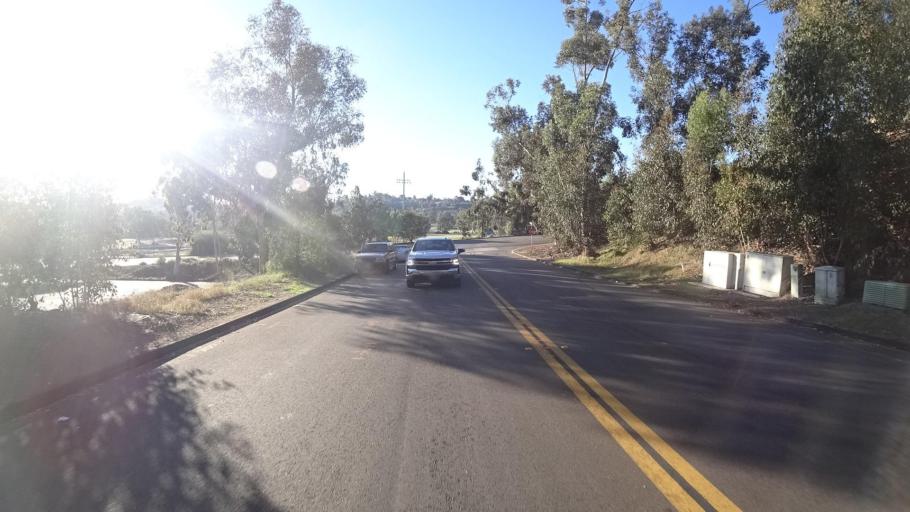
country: US
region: California
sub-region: San Diego County
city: Bonita
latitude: 32.6676
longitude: -117.0289
